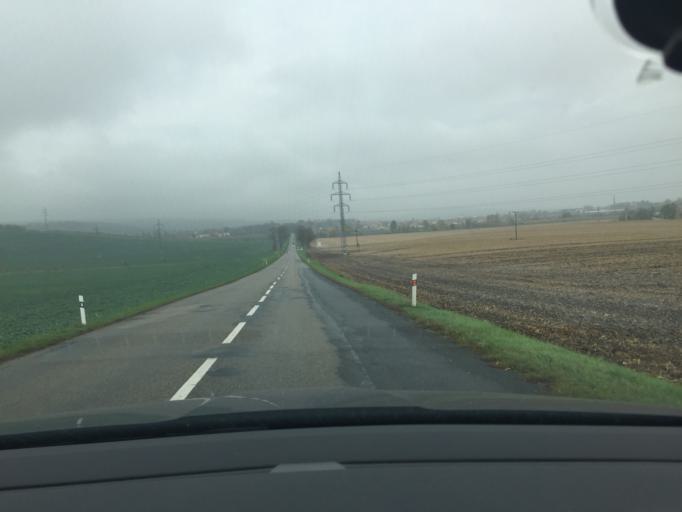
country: CZ
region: South Moravian
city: Krenovice
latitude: 49.1480
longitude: 16.8482
